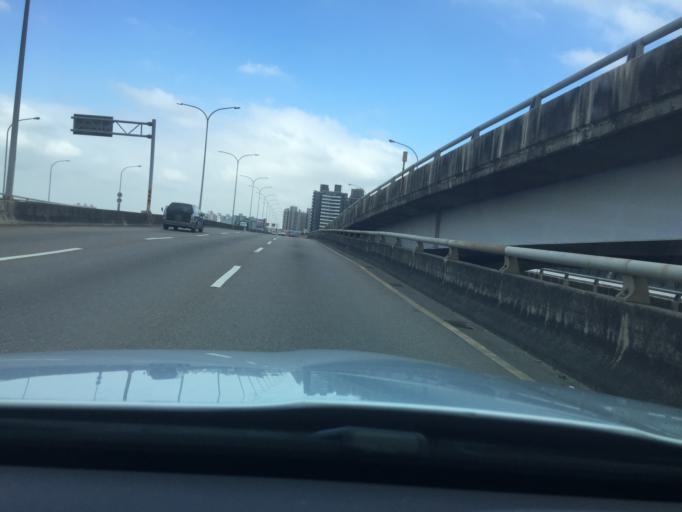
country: TW
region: Taiwan
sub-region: Hsinchu
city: Zhubei
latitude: 24.8211
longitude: 120.9961
